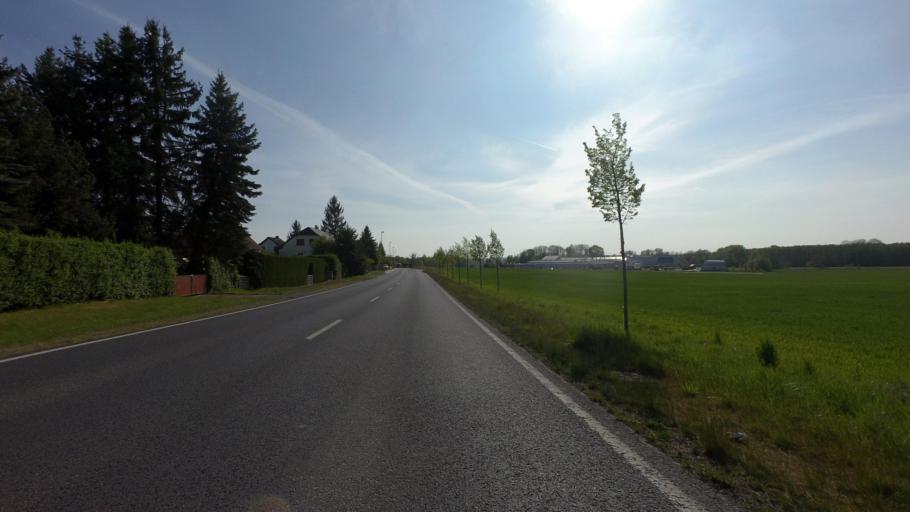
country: DE
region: Saxony
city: Arnsdorf
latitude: 51.1286
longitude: 13.9521
